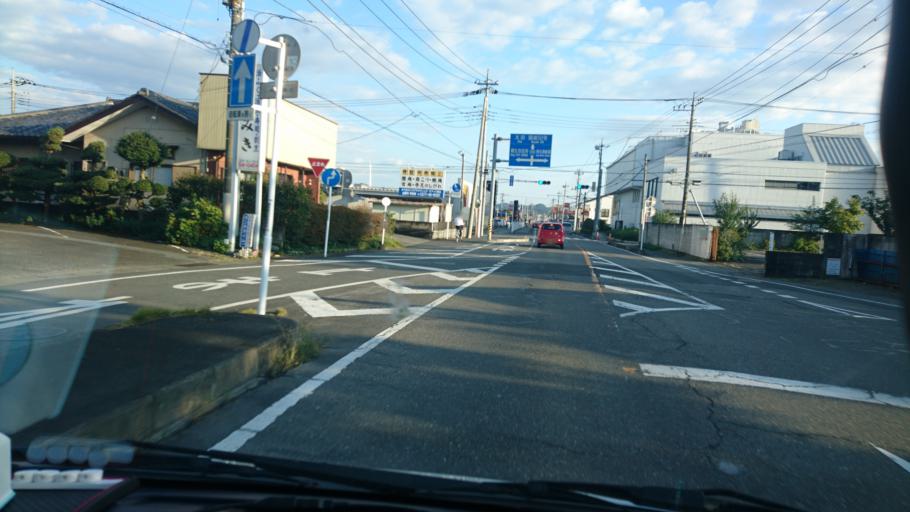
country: JP
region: Gunma
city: Kiryu
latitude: 36.4060
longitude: 139.3160
